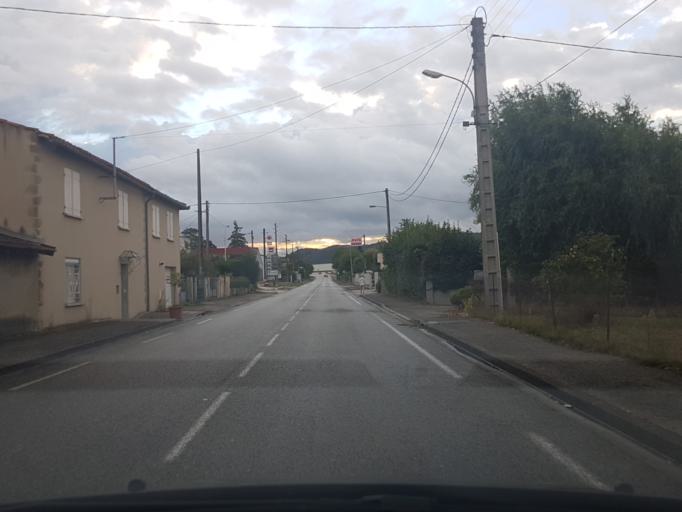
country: FR
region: Midi-Pyrenees
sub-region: Departement de l'Ariege
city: Mirepoix
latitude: 43.0886
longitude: 1.8686
